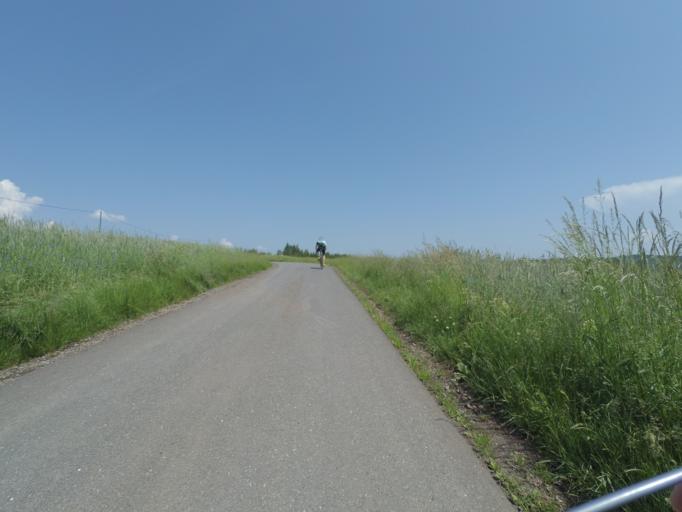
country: DE
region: Rheinland-Pfalz
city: Monreal
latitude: 50.3036
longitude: 7.1621
